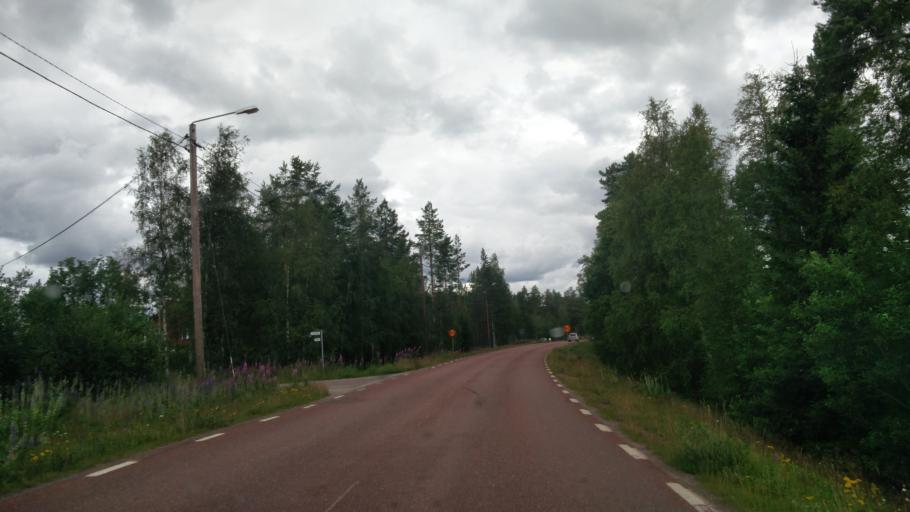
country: NO
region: Hedmark
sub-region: Trysil
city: Innbygda
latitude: 61.1377
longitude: 12.8075
